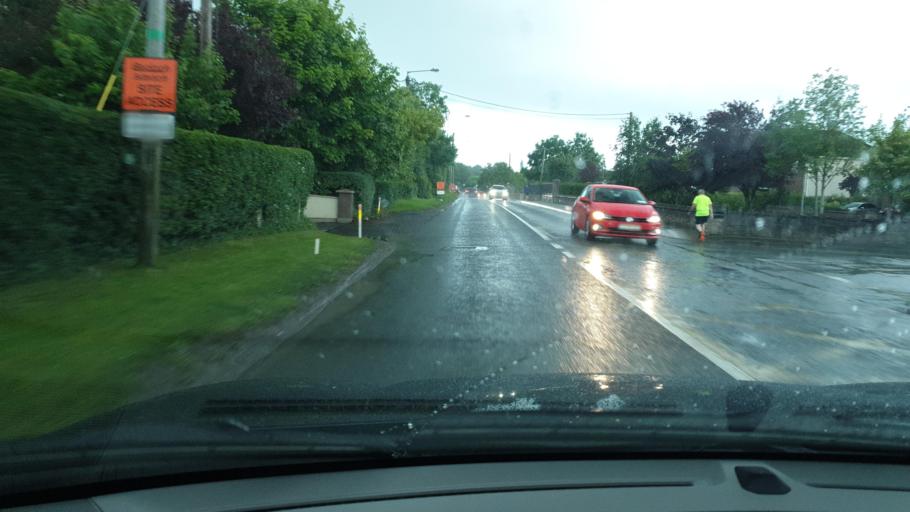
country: IE
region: Leinster
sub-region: An Mhi
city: Navan
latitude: 53.6405
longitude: -6.6886
